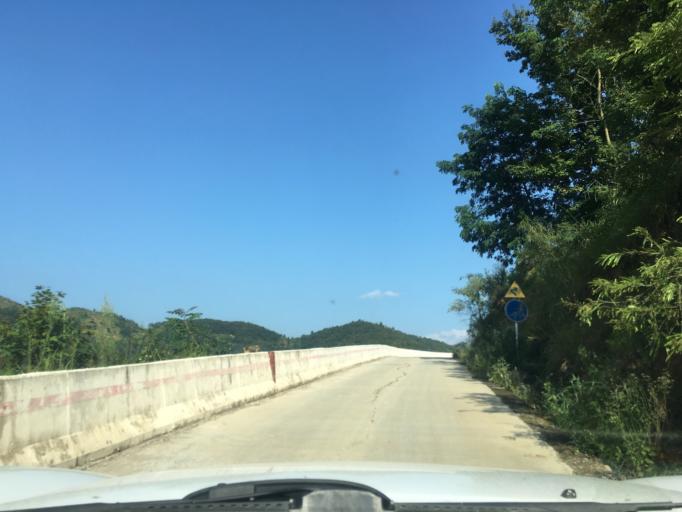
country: CN
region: Guangxi Zhuangzu Zizhiqu
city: Xinzhou
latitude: 25.4419
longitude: 105.7481
